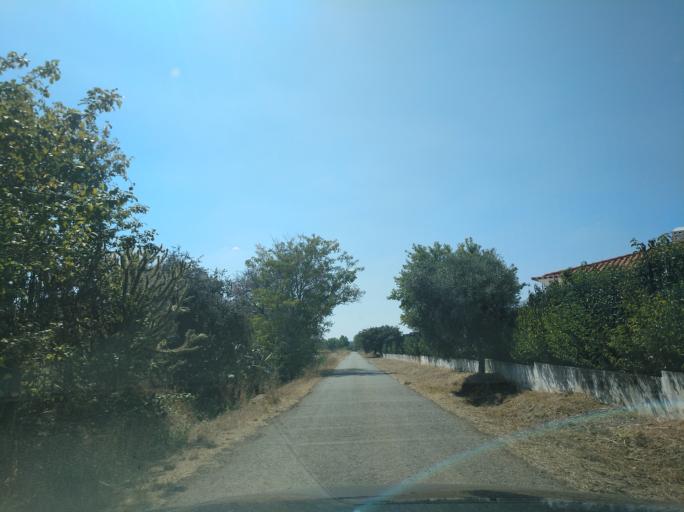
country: PT
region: Portalegre
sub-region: Campo Maior
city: Campo Maior
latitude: 39.0251
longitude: -7.0936
